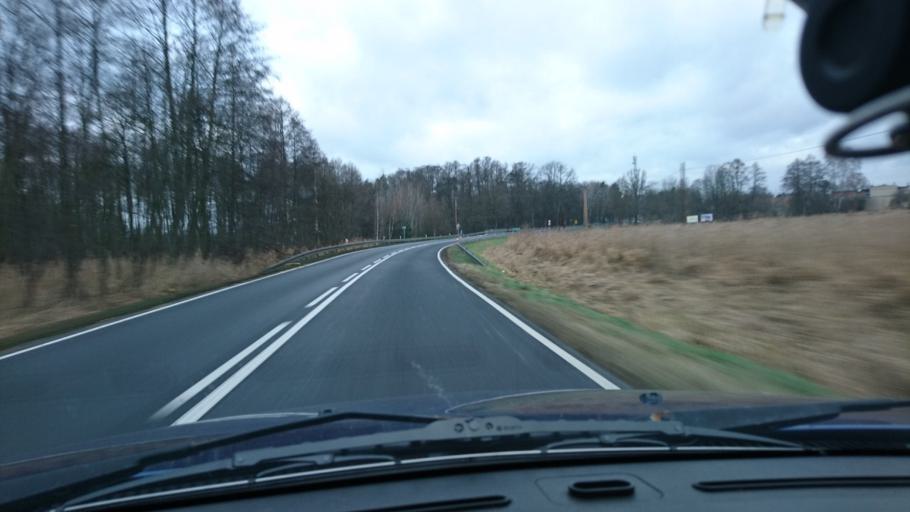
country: PL
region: Opole Voivodeship
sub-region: Powiat kluczborski
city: Kluczbork
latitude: 50.9535
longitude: 18.3096
